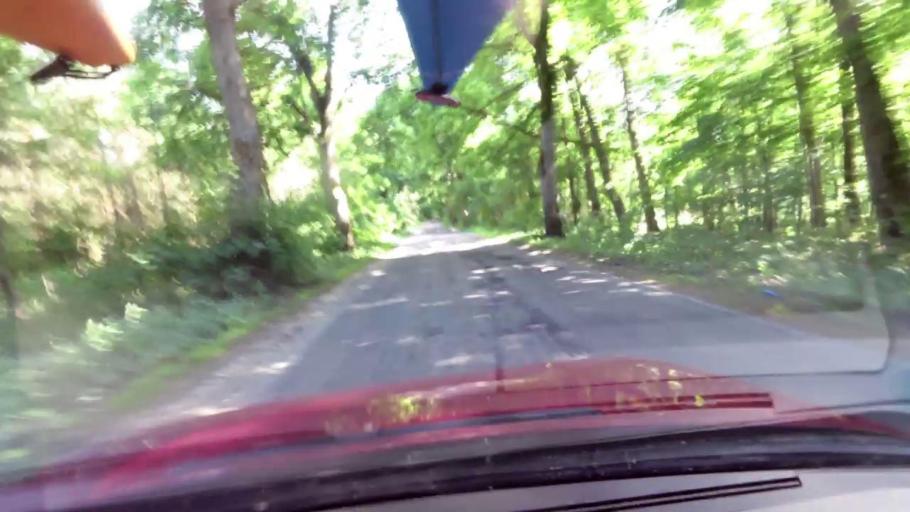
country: PL
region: Pomeranian Voivodeship
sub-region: Powiat slupski
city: Kepice
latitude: 54.1636
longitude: 16.9064
